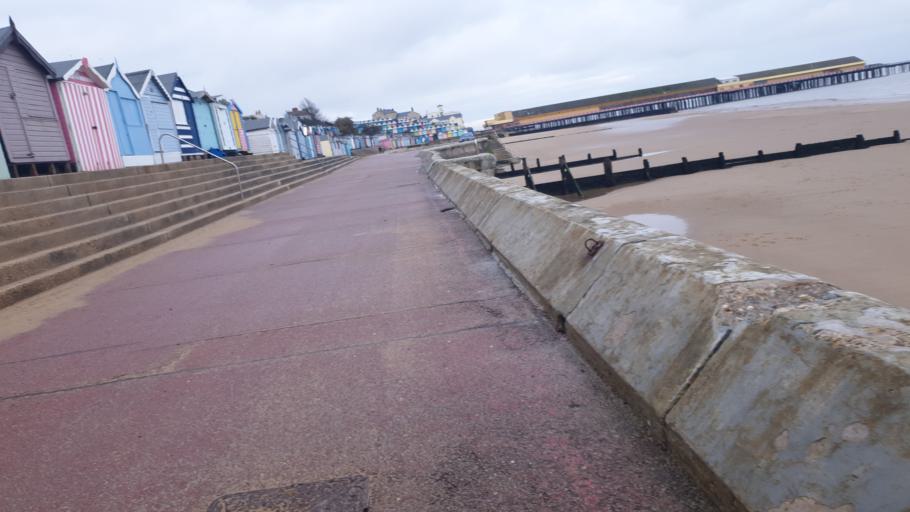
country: GB
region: England
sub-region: Essex
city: Walton-on-the-Naze
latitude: 51.8436
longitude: 1.2675
